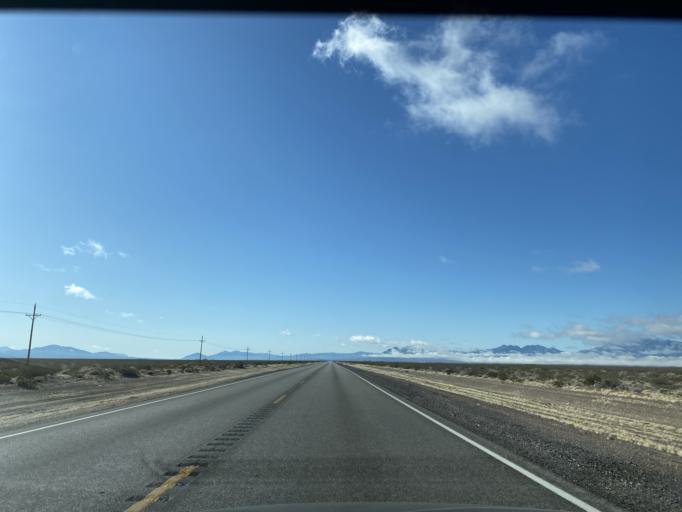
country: US
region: Nevada
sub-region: Nye County
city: Beatty
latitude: 36.6088
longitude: -116.4066
